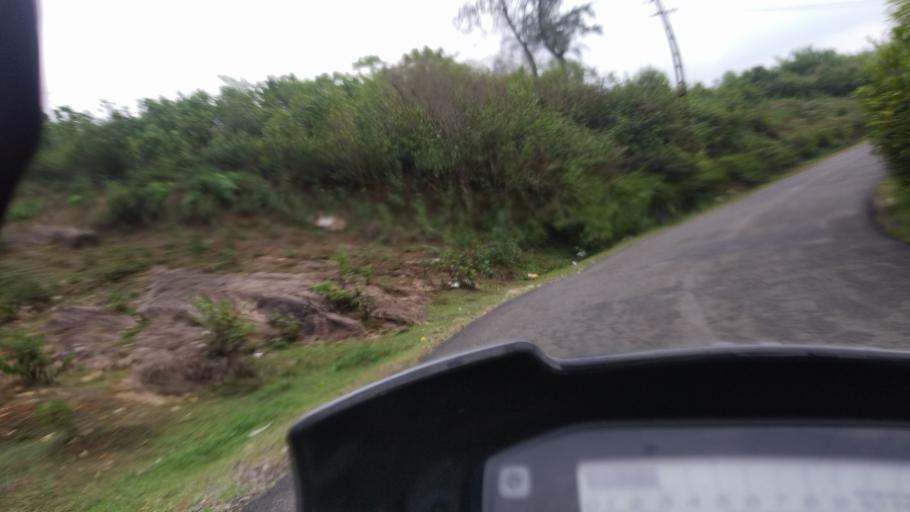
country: IN
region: Kerala
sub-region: Kottayam
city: Erattupetta
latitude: 9.6350
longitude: 76.9491
